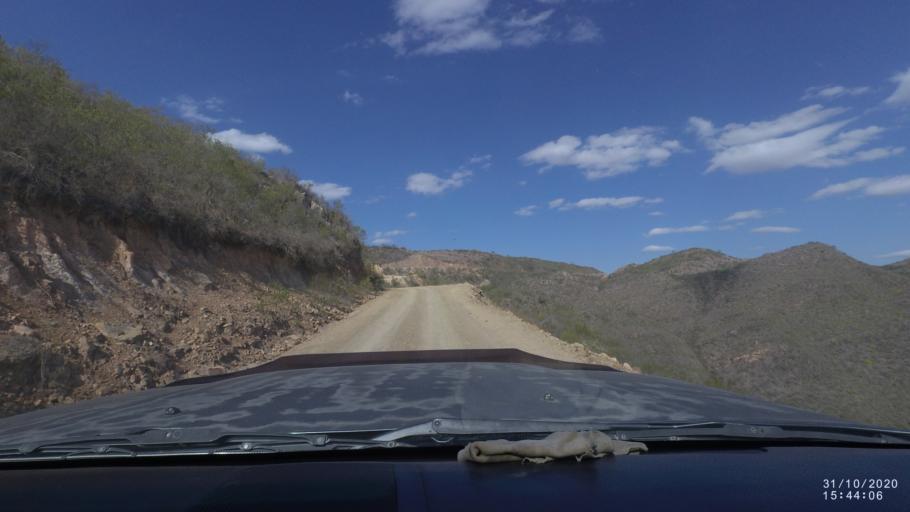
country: BO
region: Chuquisaca
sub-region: Provincia Zudanez
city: Mojocoya
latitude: -18.3193
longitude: -64.7251
